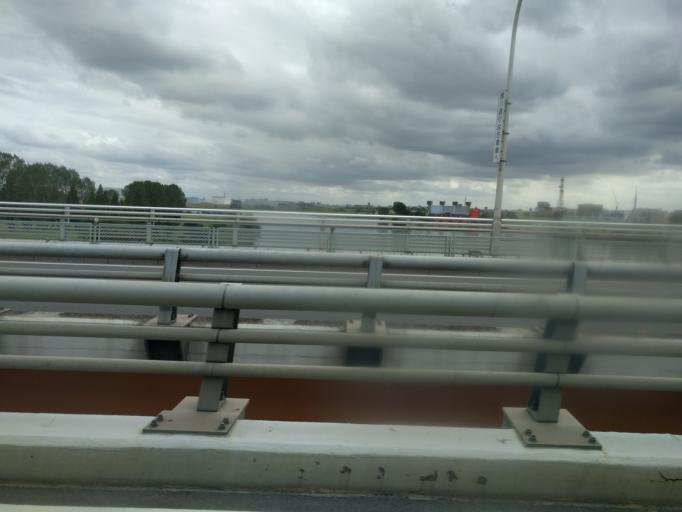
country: JP
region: Saitama
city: Kawaguchi
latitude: 35.7899
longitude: 139.7242
